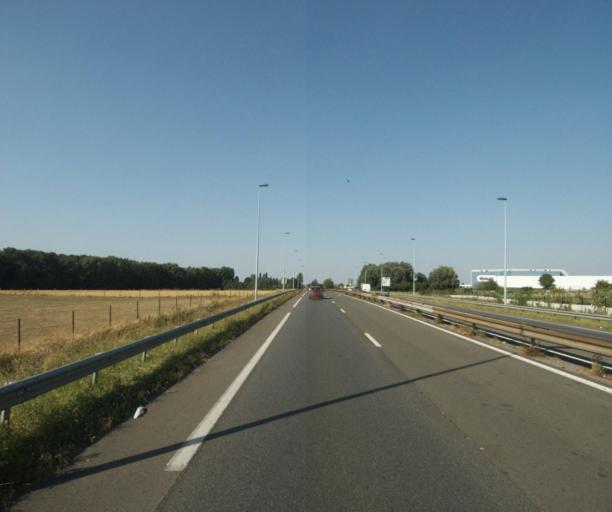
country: FR
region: Nord-Pas-de-Calais
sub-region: Departement du Nord
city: Hem
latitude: 50.6599
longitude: 3.1751
